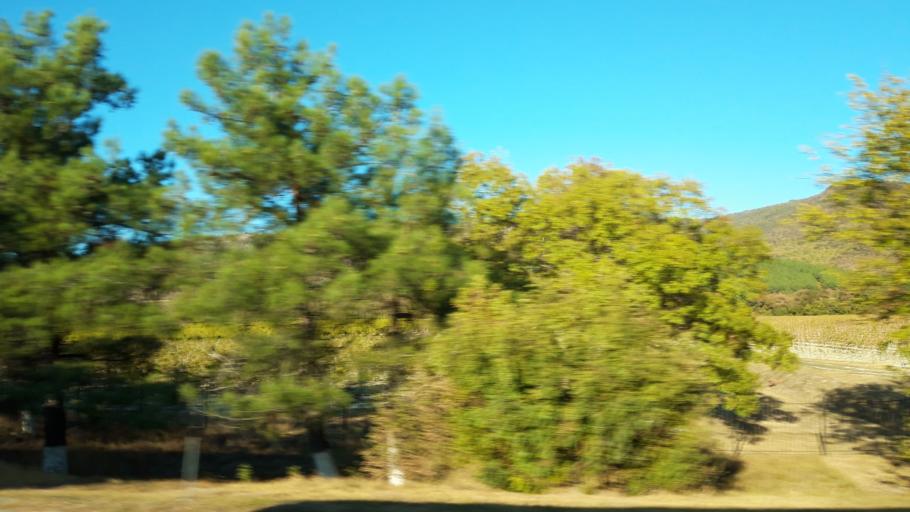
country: RU
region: Krasnodarskiy
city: Kabardinka
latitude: 44.6242
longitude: 38.0140
